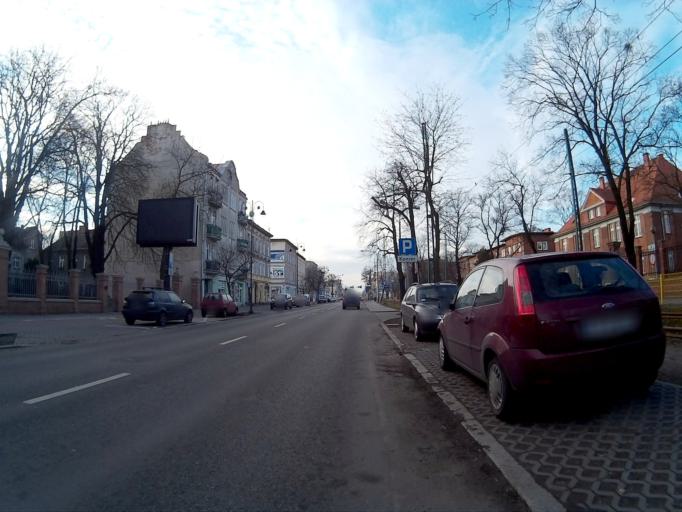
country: PL
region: Kujawsko-Pomorskie
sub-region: Bydgoszcz
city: Bydgoszcz
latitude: 53.1389
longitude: 18.0169
